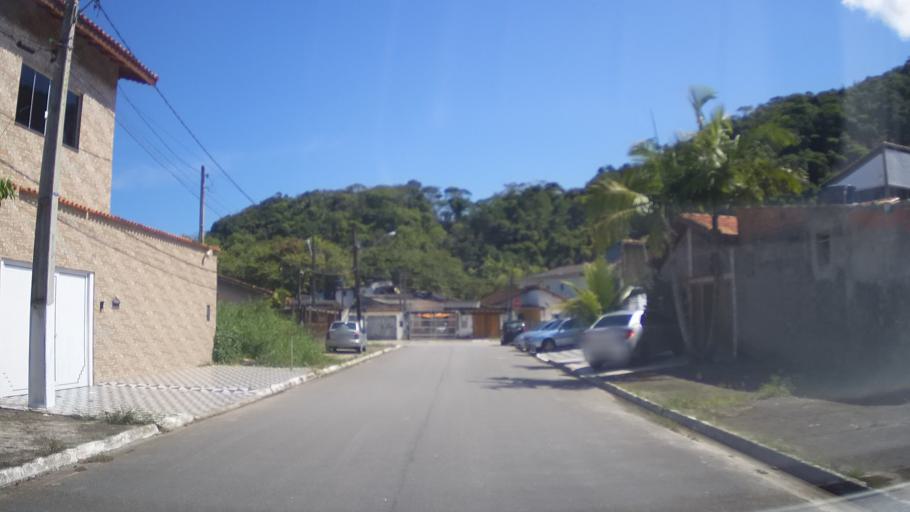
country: BR
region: Sao Paulo
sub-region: Mongagua
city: Mongagua
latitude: -24.0838
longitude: -46.6065
